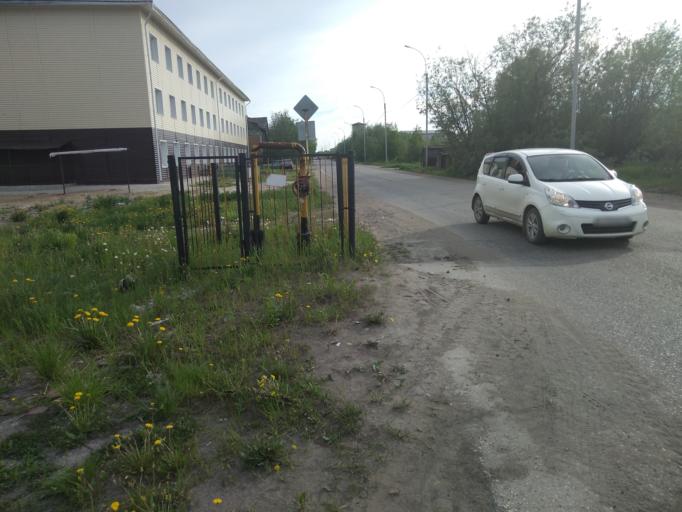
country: RU
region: Komi Republic
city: Pechora
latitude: 65.1501
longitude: 57.2183
